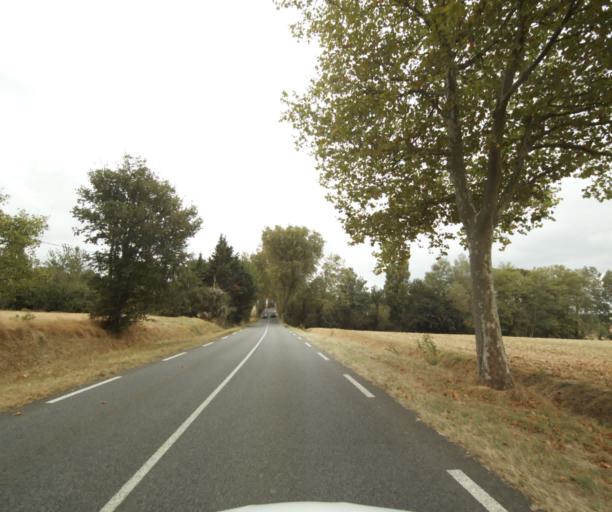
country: FR
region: Midi-Pyrenees
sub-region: Departement de la Haute-Garonne
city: Villefranche-de-Lauragais
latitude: 43.4156
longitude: 1.7412
